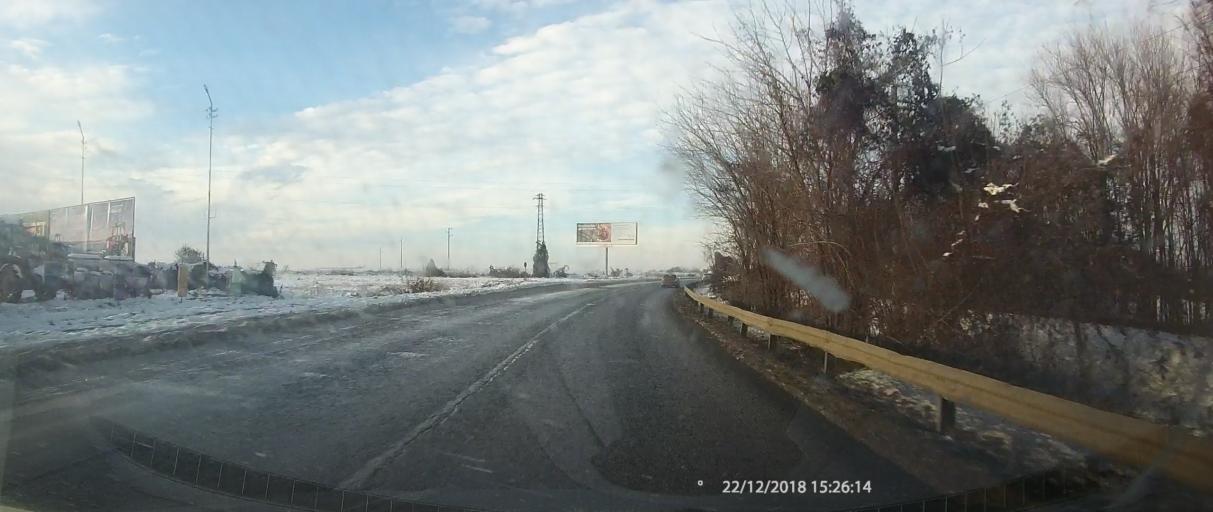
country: RO
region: Giurgiu
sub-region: Comuna Slobozia
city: Slobozia
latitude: 43.7698
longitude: 25.8988
